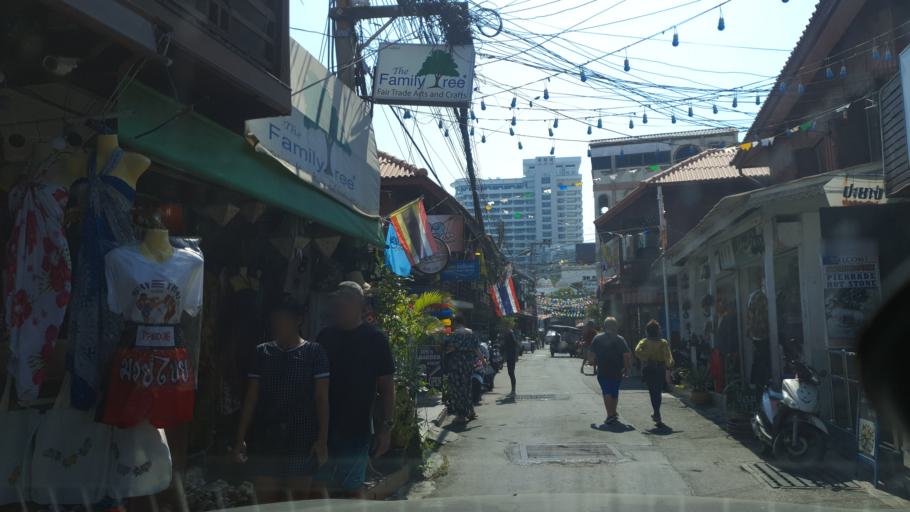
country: TH
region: Prachuap Khiri Khan
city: Hua Hin
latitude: 12.5731
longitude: 99.9595
